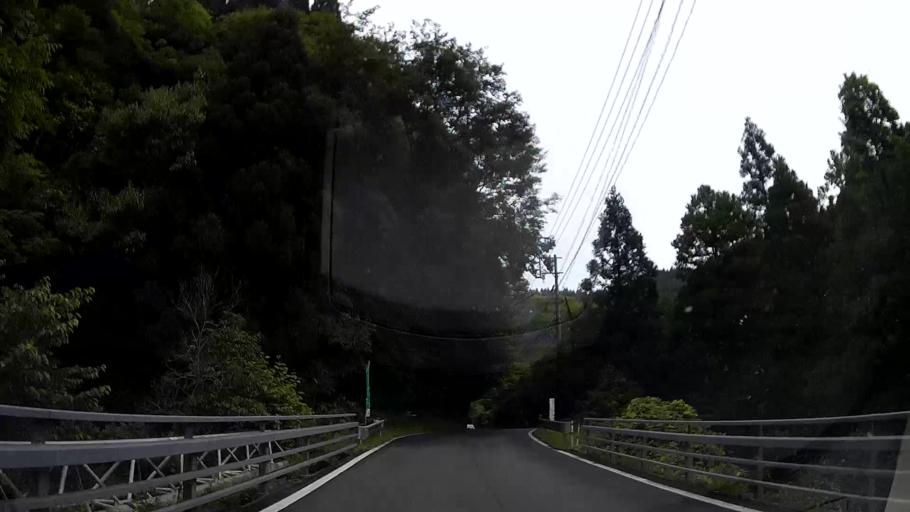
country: JP
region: Kumamoto
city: Kikuchi
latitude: 33.1033
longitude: 130.9607
